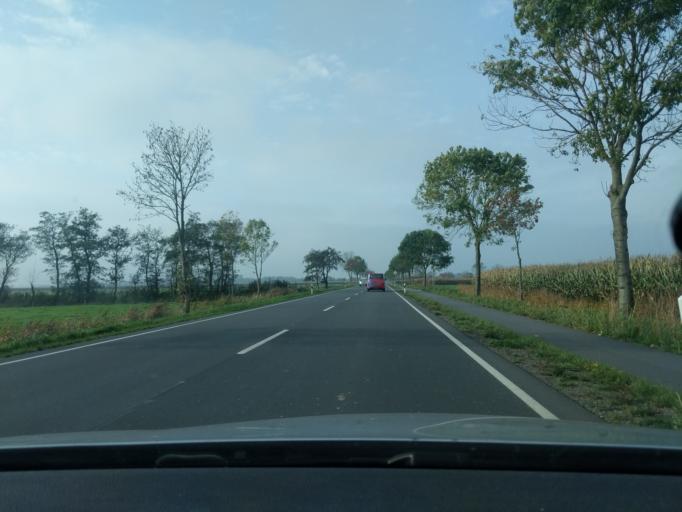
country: DE
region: Lower Saxony
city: Belum
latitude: 53.8196
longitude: 8.9745
